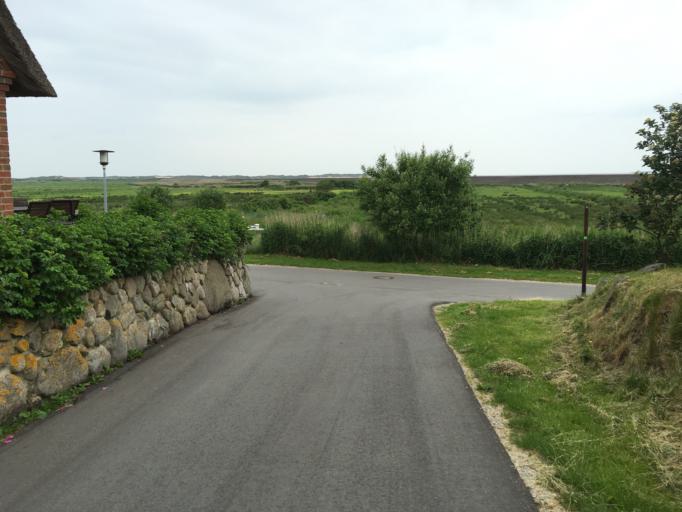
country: DE
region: Schleswig-Holstein
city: Norddorf
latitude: 54.6802
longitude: 8.3374
